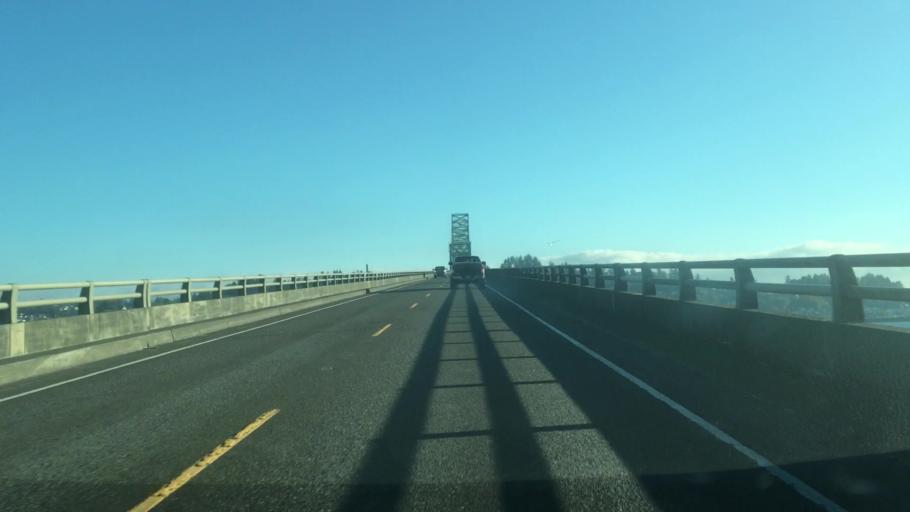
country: US
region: Oregon
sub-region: Clatsop County
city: Astoria
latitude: 46.2015
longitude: -123.8550
